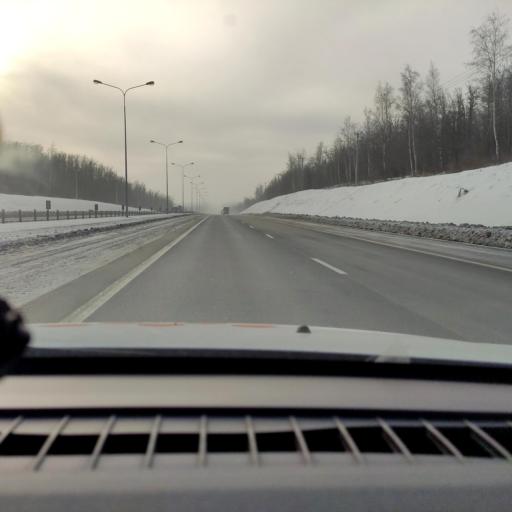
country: RU
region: Samara
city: Novosemeykino
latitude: 53.3644
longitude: 50.3078
